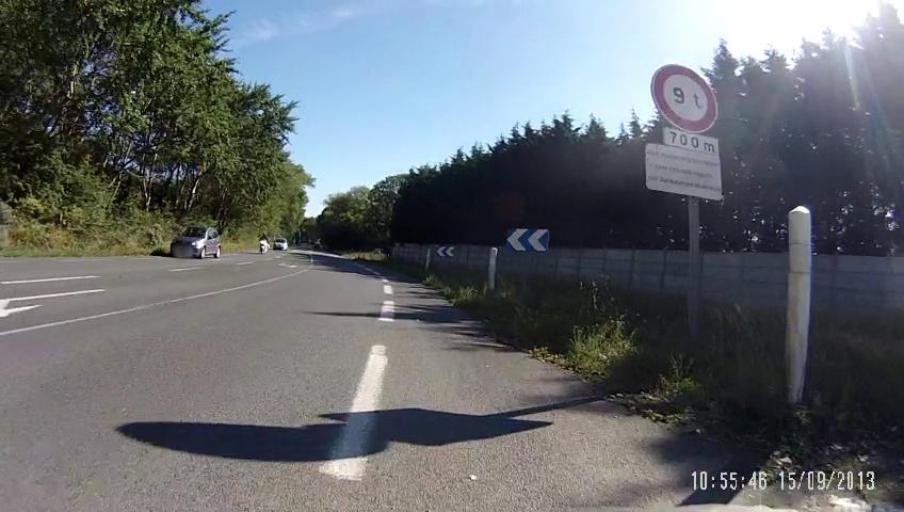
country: FR
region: Nord-Pas-de-Calais
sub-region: Departement du Nord
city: Zuydcoote
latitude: 51.0574
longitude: 2.4725
